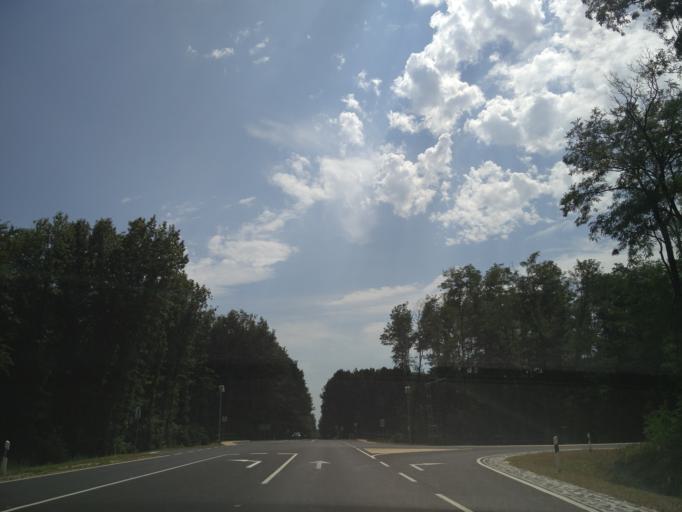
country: HU
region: Zala
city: Zalaegerszeg
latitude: 46.9091
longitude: 16.8588
